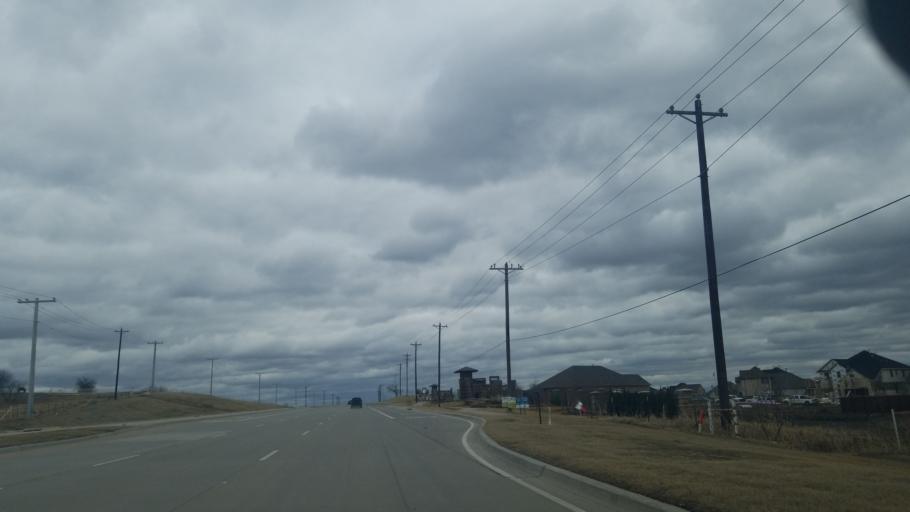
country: US
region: Texas
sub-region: Denton County
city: Roanoke
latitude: 33.0604
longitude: -97.2173
